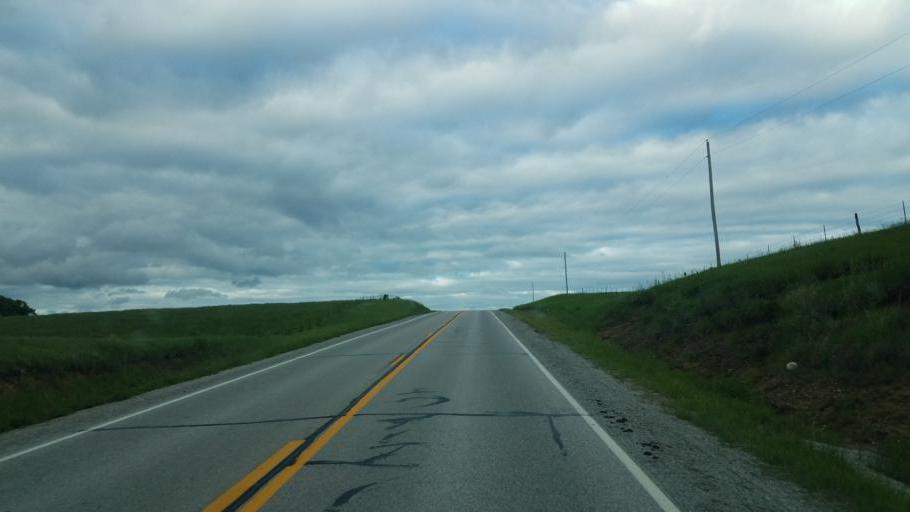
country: US
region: Iowa
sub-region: Decatur County
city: Lamoni
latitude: 40.6237
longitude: -93.8776
